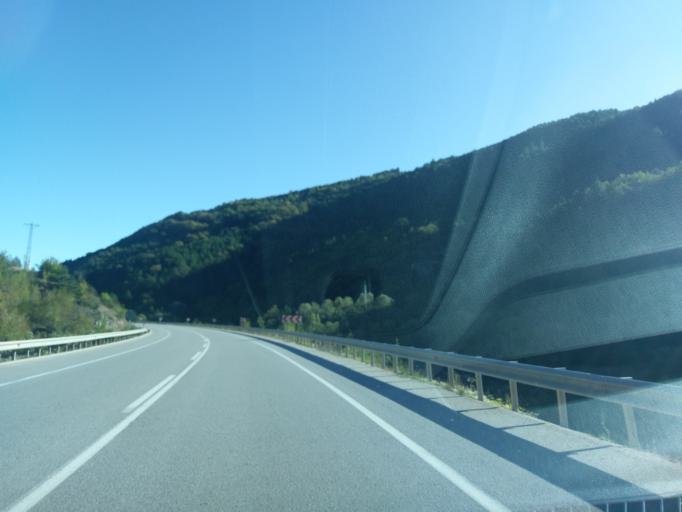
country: TR
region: Sinop
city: Erfelek
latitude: 41.7125
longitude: 34.9316
